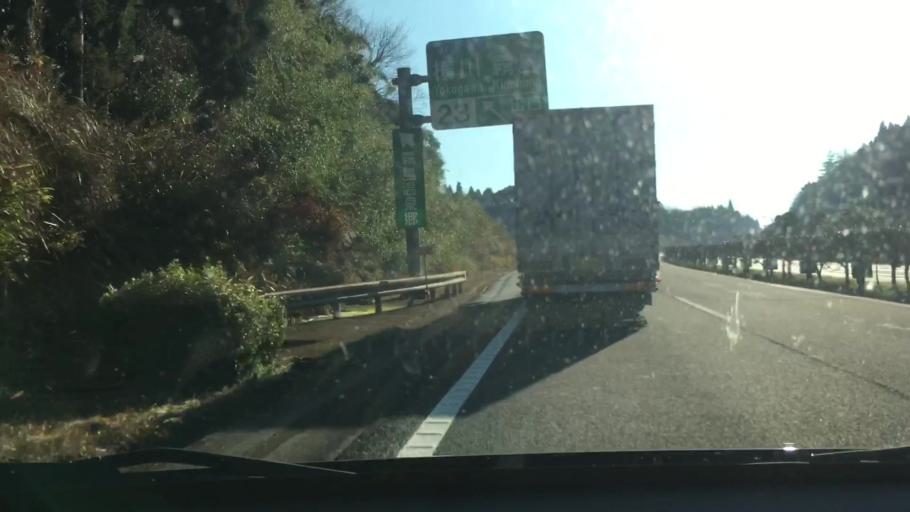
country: JP
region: Kagoshima
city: Kajiki
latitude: 31.8987
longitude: 130.7060
